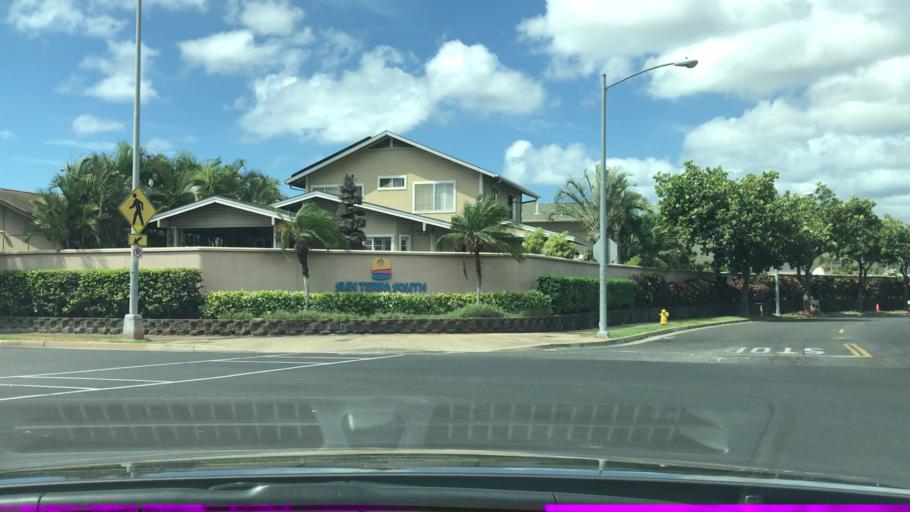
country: US
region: Hawaii
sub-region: Honolulu County
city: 'Ewa Gentry
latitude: 21.3341
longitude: -158.0289
